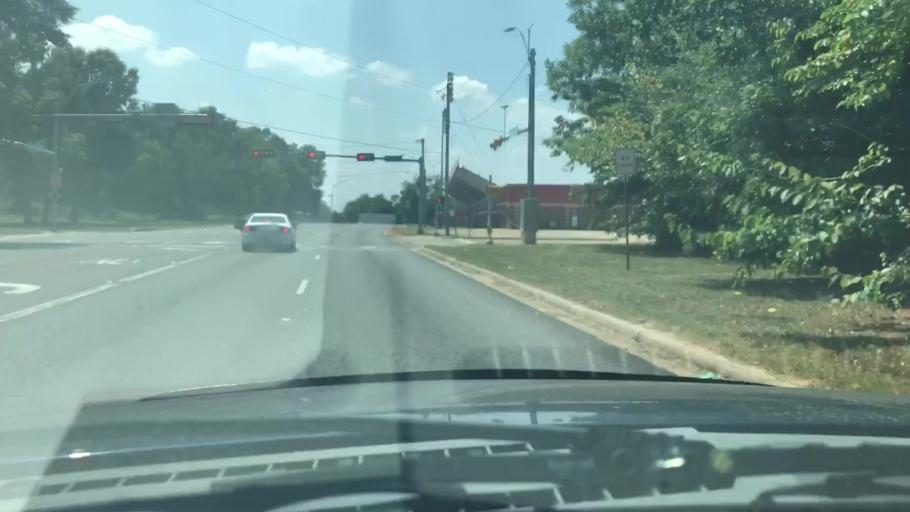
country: US
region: Texas
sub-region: Bowie County
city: Texarkana
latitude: 33.4297
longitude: -94.0615
